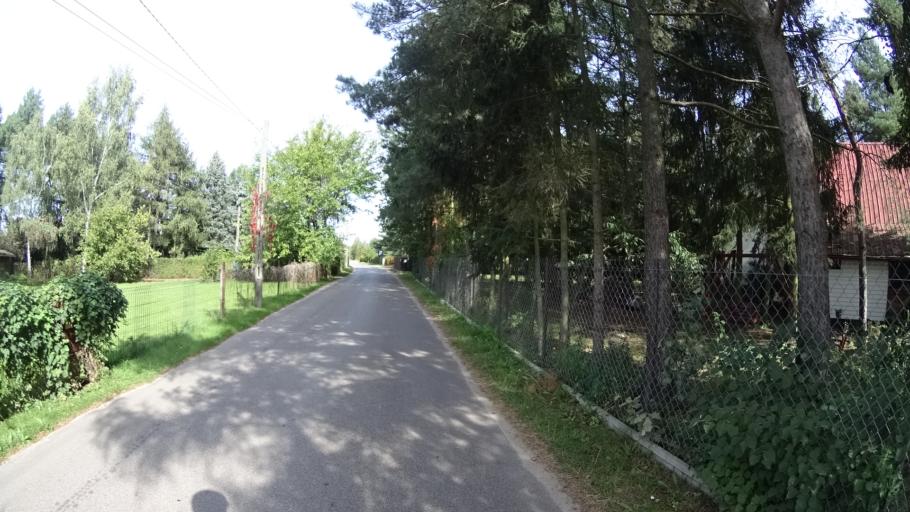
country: PL
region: Masovian Voivodeship
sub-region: Powiat legionowski
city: Serock
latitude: 52.4858
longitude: 21.0798
